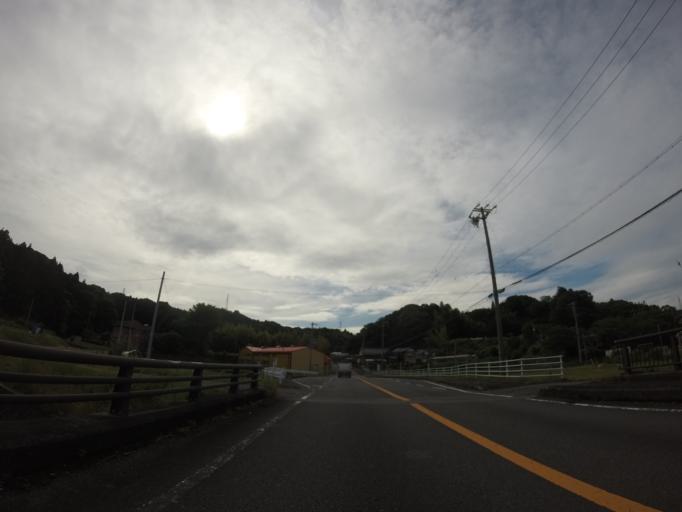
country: JP
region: Shizuoka
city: Shimada
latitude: 34.7862
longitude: 138.1537
